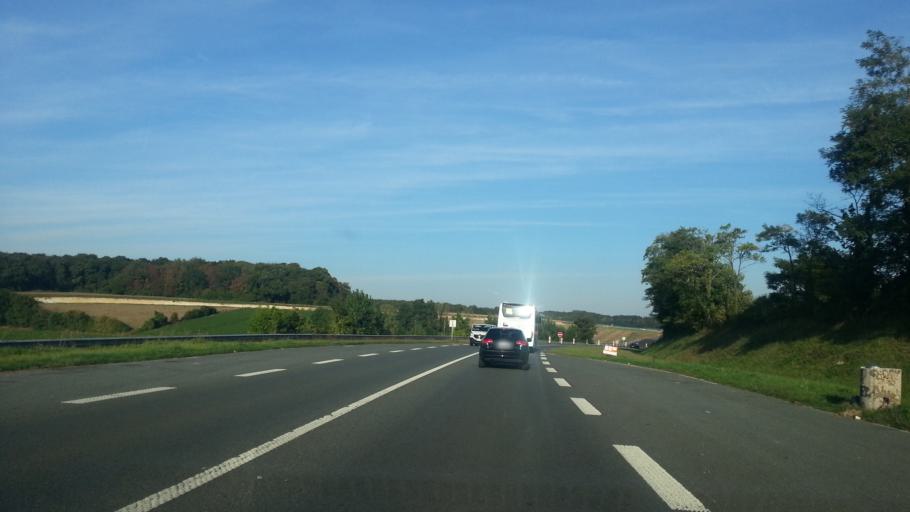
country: FR
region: Picardie
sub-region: Departement de l'Oise
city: Beauvais
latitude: 49.4595
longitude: 2.0819
